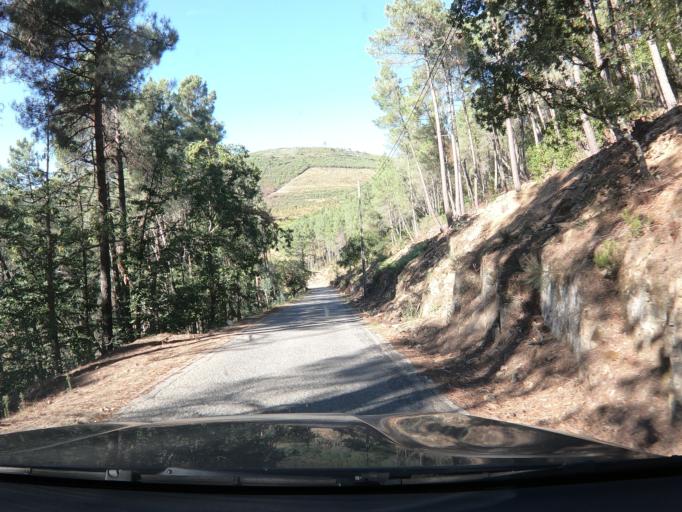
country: PT
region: Vila Real
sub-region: Sabrosa
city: Vilela
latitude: 41.2226
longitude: -7.5821
